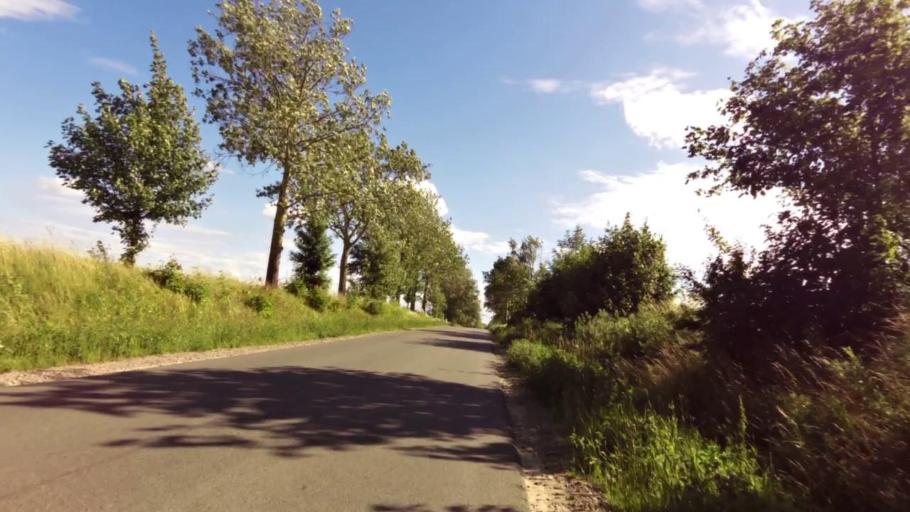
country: PL
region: West Pomeranian Voivodeship
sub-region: Powiat slawienski
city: Slawno
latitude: 54.4438
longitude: 16.7351
